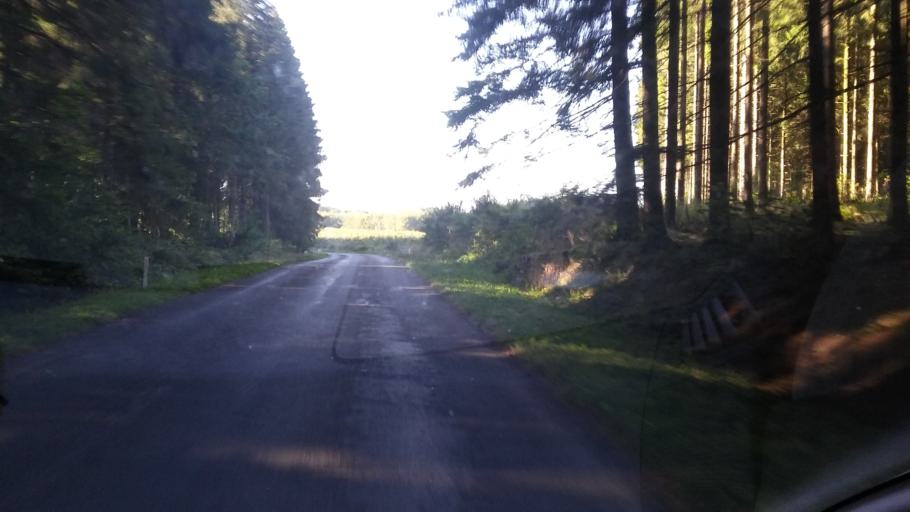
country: BE
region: Wallonia
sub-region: Province du Luxembourg
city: Neufchateau
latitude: 49.8113
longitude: 5.4140
